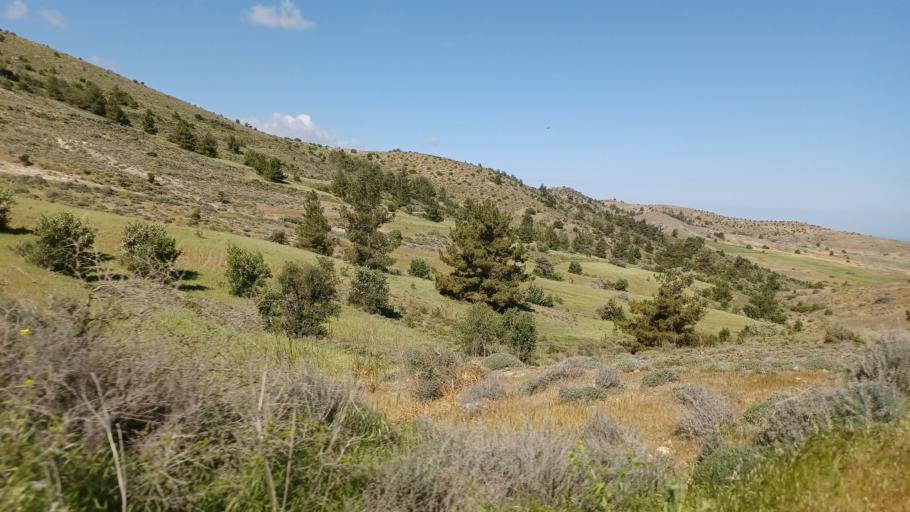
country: CY
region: Lefkosia
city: Peristerona
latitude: 35.0640
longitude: 33.0524
